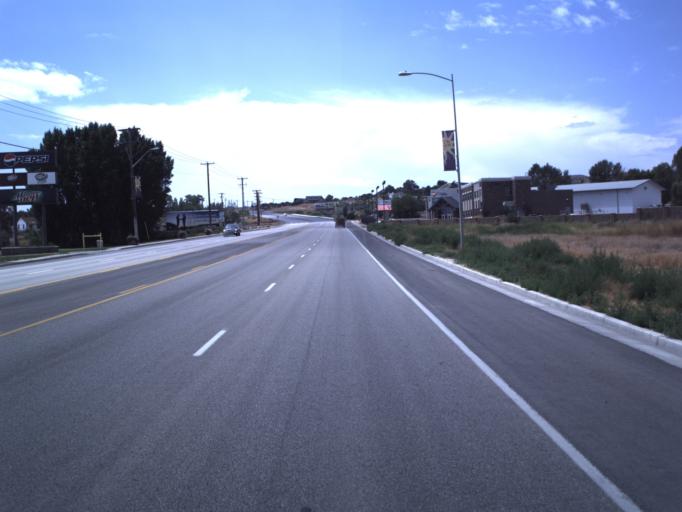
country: US
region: Utah
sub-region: Uintah County
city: Maeser
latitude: 40.4357
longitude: -109.5699
